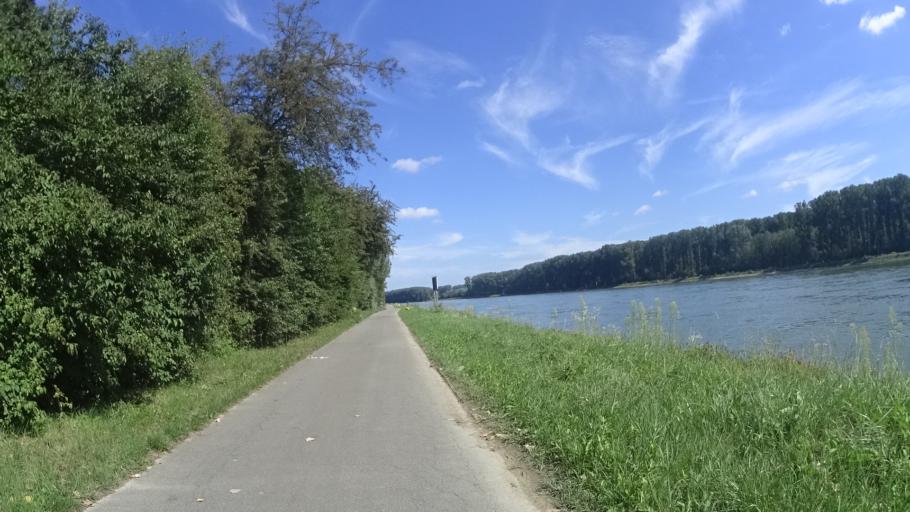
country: DE
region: Rheinland-Pfalz
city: Germersheim
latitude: 49.2015
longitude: 8.3840
